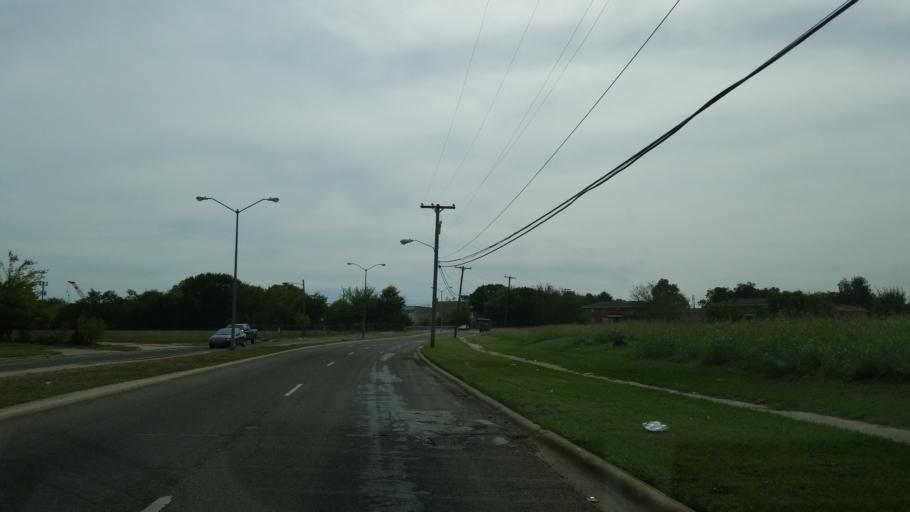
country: US
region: Texas
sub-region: Dallas County
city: Dallas
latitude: 32.7716
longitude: -96.7380
